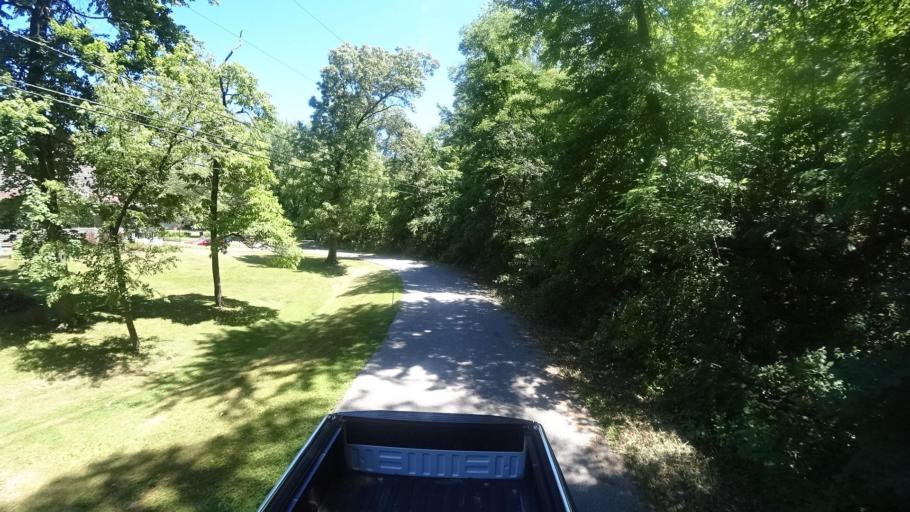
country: US
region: Indiana
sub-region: Porter County
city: Porter
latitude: 41.6394
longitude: -87.0655
